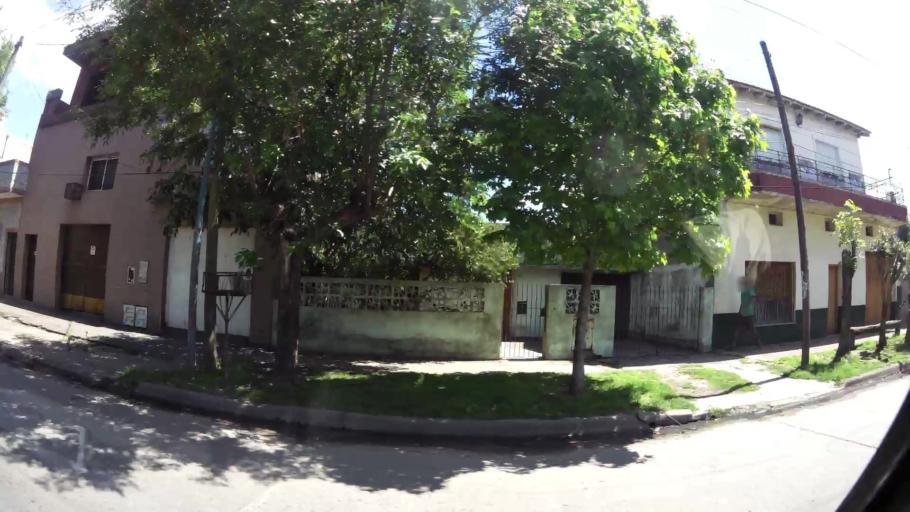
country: AR
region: Buenos Aires
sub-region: Partido de Lanus
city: Lanus
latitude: -34.6915
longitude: -58.4282
